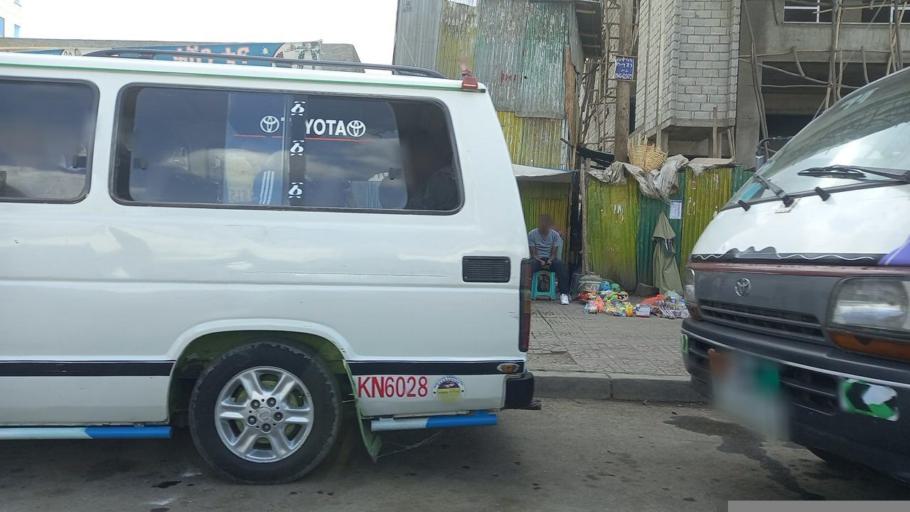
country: ET
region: Adis Abeba
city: Addis Ababa
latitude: 8.9605
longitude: 38.7128
